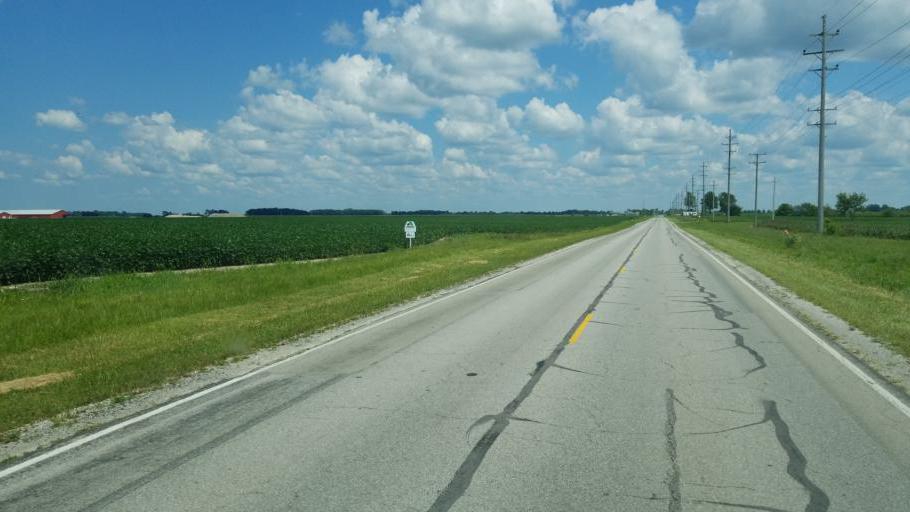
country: US
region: Ohio
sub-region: Marion County
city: Marion
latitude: 40.6303
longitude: -83.0645
